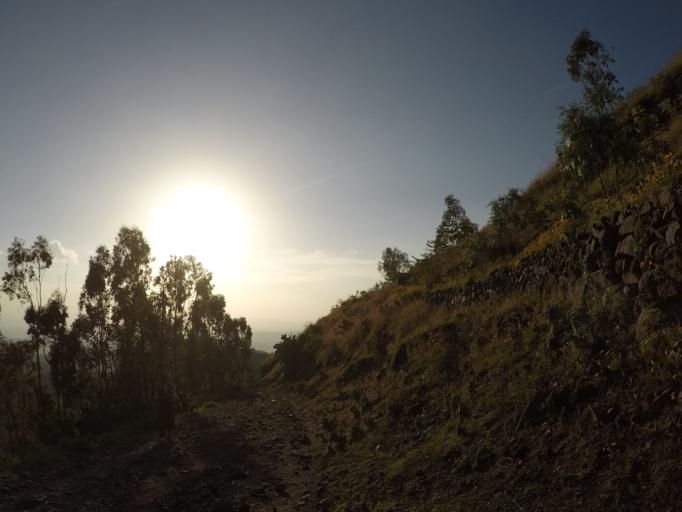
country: ET
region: Amhara
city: Lalibela
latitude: 12.0339
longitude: 39.0528
